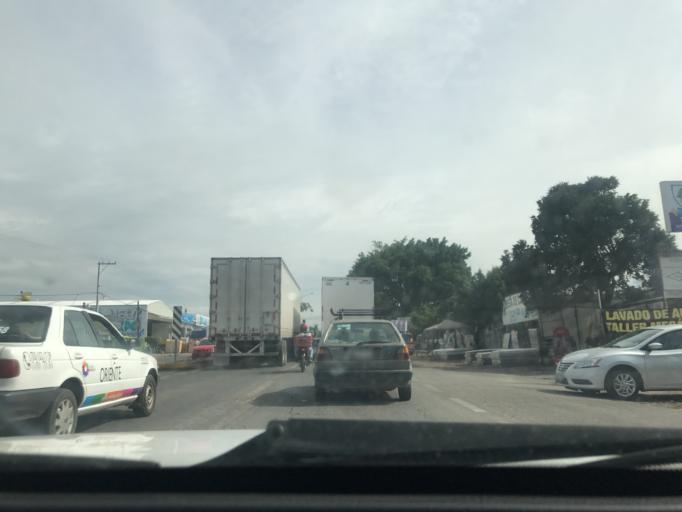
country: MX
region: Morelos
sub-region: Cuautla
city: Tierra Larga (Campo Nuevo)
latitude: 18.8610
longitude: -98.9330
